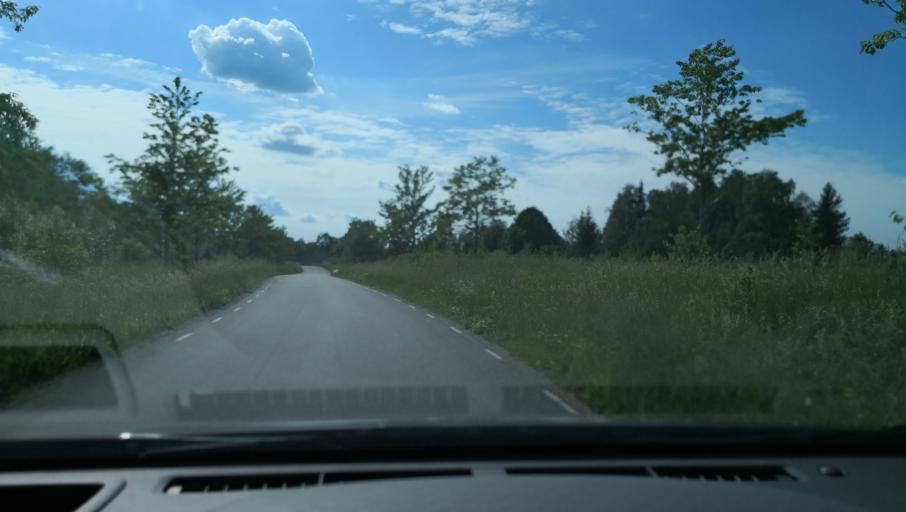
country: SE
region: Uppsala
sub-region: Enkopings Kommun
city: Orsundsbro
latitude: 59.8163
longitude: 17.3654
